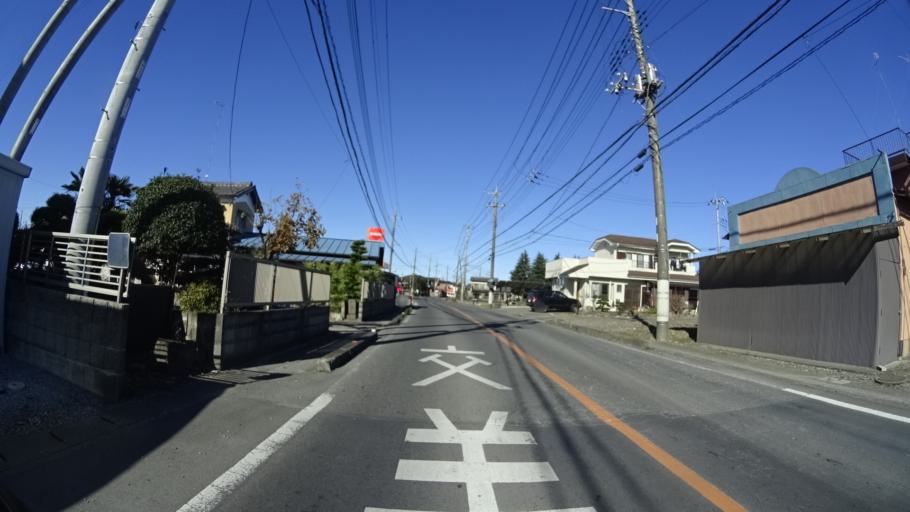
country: JP
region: Tochigi
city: Tochigi
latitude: 36.4214
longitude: 139.7497
